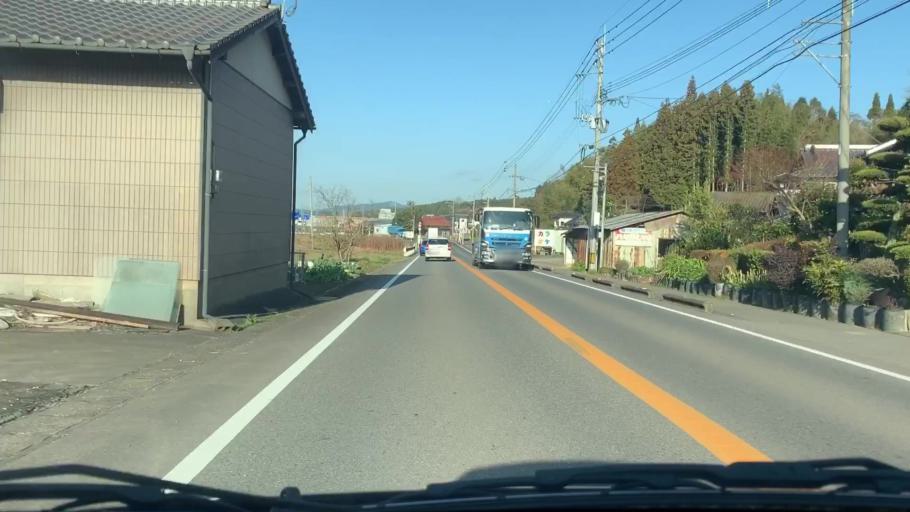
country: JP
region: Saga Prefecture
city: Takeocho-takeo
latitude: 33.2487
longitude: 130.0020
